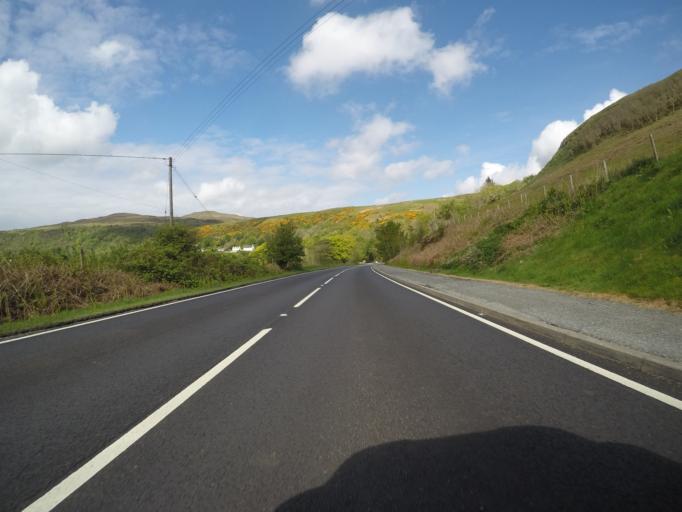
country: GB
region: Scotland
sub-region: Highland
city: Portree
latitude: 57.5872
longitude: -6.3564
